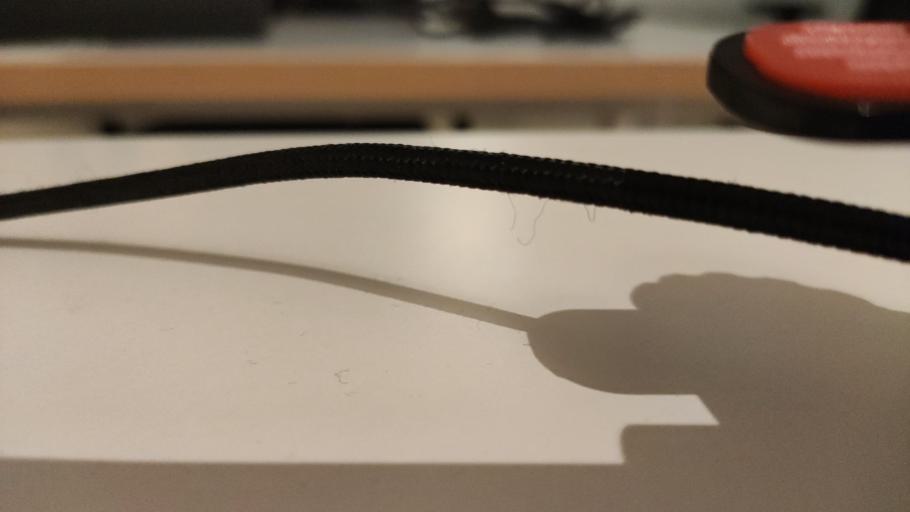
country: RU
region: Moskovskaya
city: Il'inskiy Pogost
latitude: 55.5173
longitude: 38.8717
